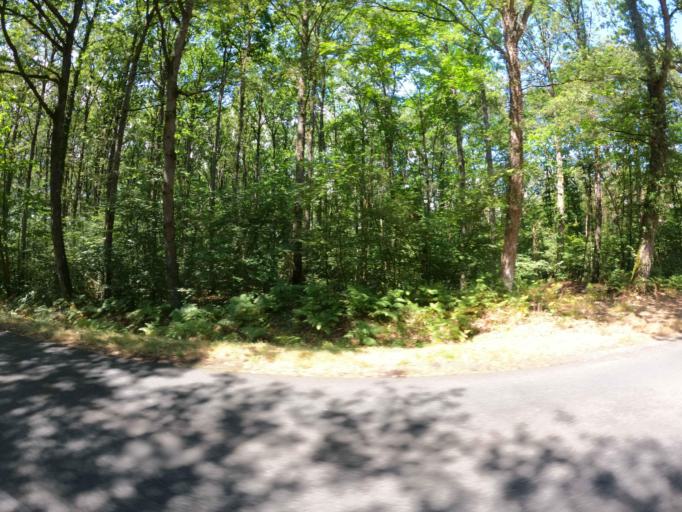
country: FR
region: Pays de la Loire
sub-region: Departement de Maine-et-Loire
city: Champigne
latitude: 47.6218
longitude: -0.5830
